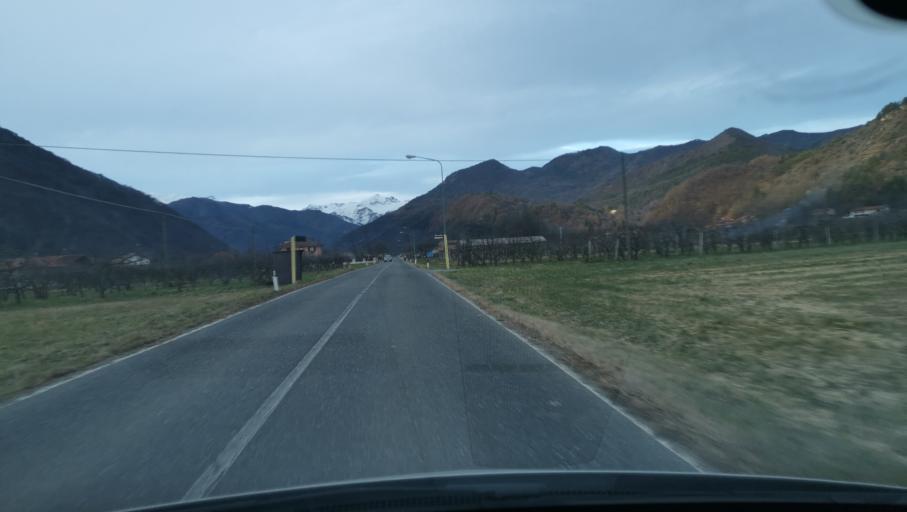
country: IT
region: Piedmont
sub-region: Provincia di Cuneo
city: Valgrana
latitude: 44.4121
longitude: 7.3696
